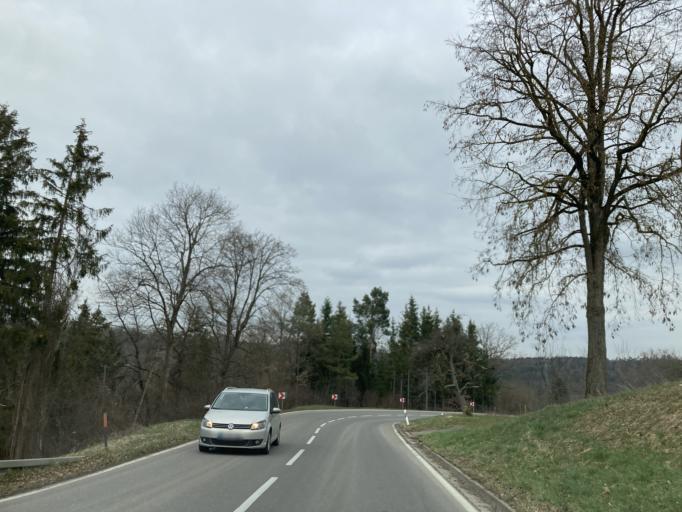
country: DE
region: Baden-Wuerttemberg
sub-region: Tuebingen Region
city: Hirrlingen
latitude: 48.4548
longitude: 8.8773
